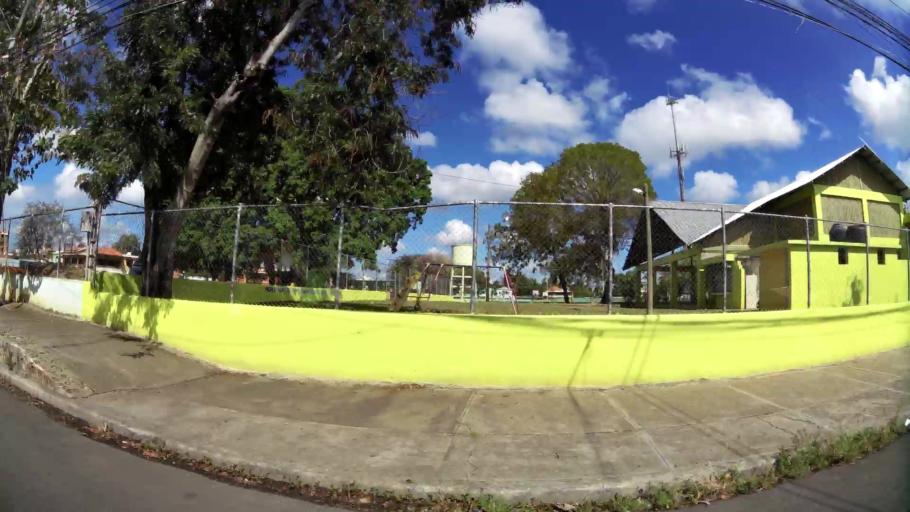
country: DO
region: Santo Domingo
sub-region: Santo Domingo
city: Santo Domingo Este
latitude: 18.5076
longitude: -69.8467
